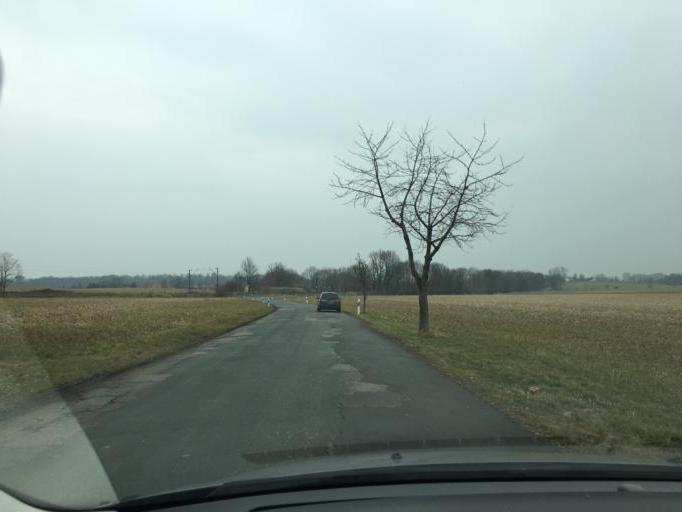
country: DE
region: Thuringia
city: Gerstenberg
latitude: 51.0347
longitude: 12.4385
